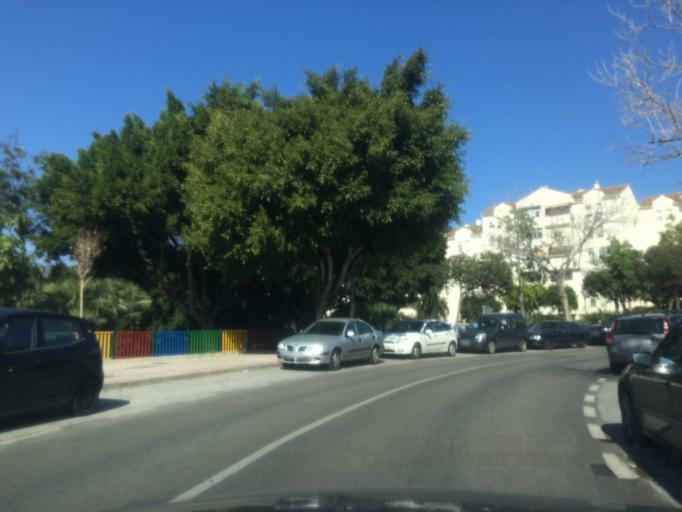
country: ES
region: Andalusia
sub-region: Provincia de Malaga
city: Malaga
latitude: 36.7450
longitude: -4.4181
